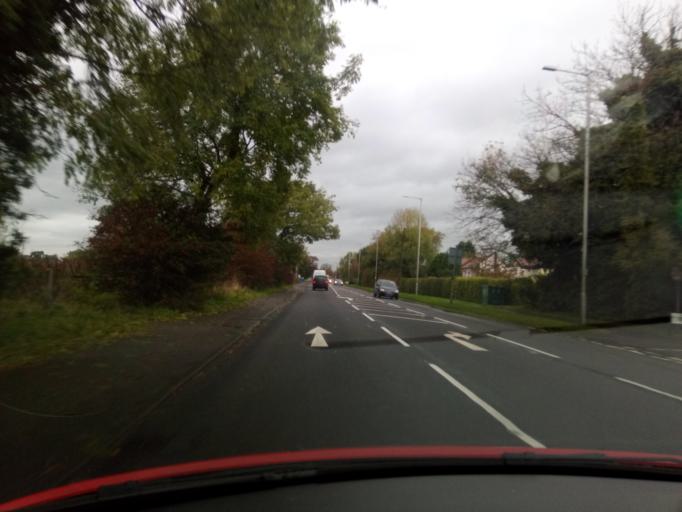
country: GB
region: England
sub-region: Lancashire
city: Catterall
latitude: 53.8339
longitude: -2.7384
